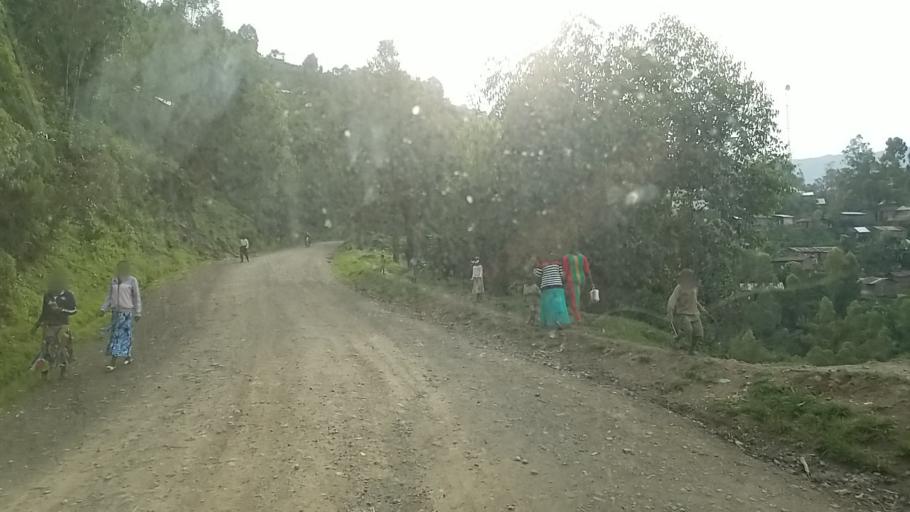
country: CD
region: Nord Kivu
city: Sake
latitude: -1.9225
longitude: 28.9436
